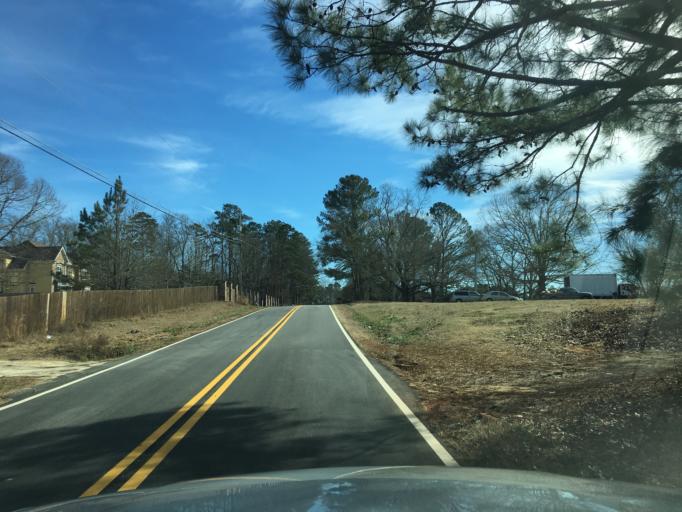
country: US
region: Georgia
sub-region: Rockdale County
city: Lakeview Estates
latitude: 33.7288
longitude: -84.0216
